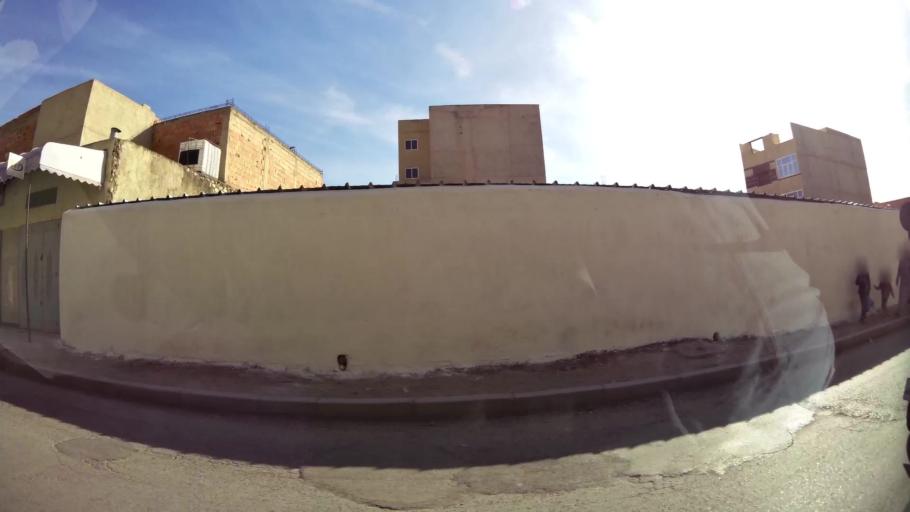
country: MA
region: Oriental
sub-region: Oujda-Angad
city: Oujda
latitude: 34.6755
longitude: -1.9036
